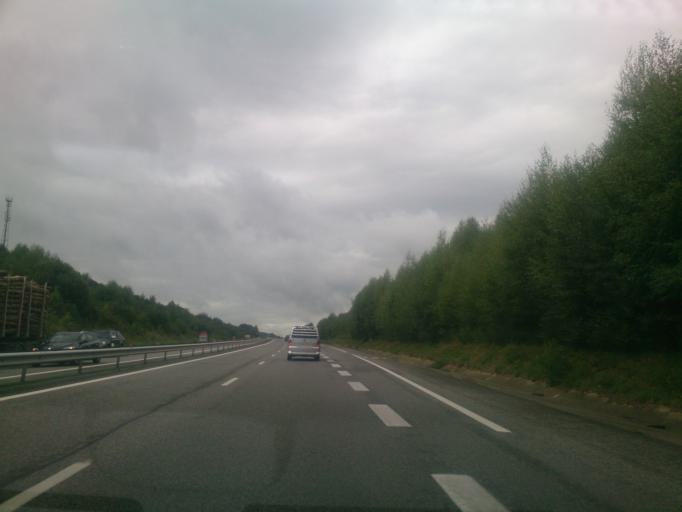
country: FR
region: Midi-Pyrenees
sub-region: Departement de la Haute-Garonne
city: Montrejeau
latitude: 43.0966
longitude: 0.5548
